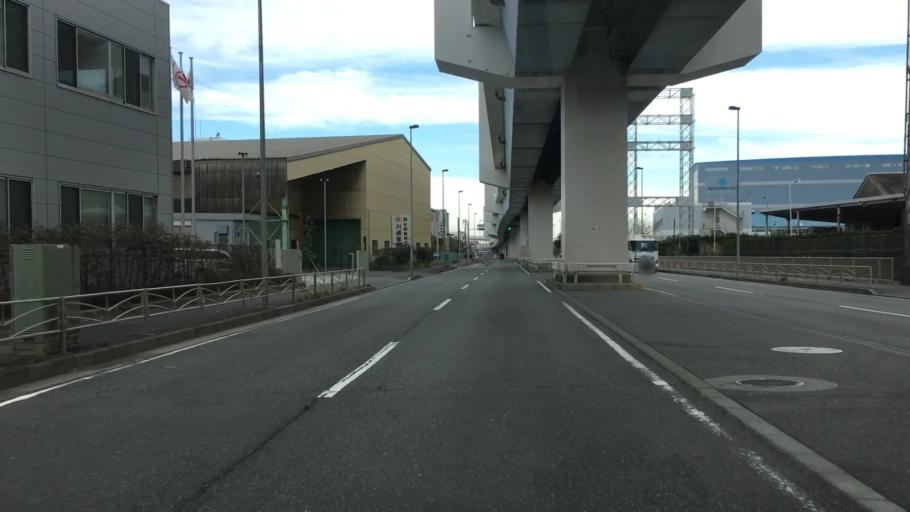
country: JP
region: Kanagawa
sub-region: Kawasaki-shi
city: Kawasaki
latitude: 35.5242
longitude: 139.7816
